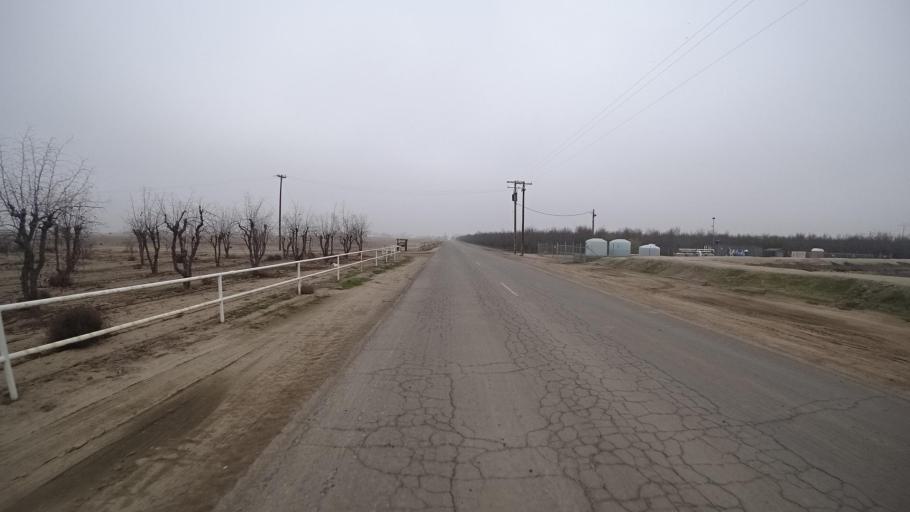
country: US
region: California
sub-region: Kern County
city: Greenfield
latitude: 35.2380
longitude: -119.1081
